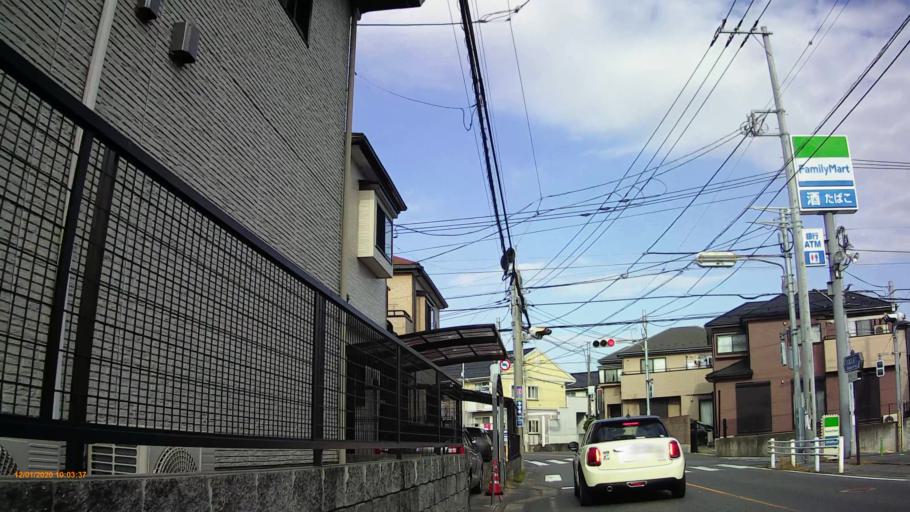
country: JP
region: Chiba
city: Yotsukaido
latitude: 35.6369
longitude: 140.1641
